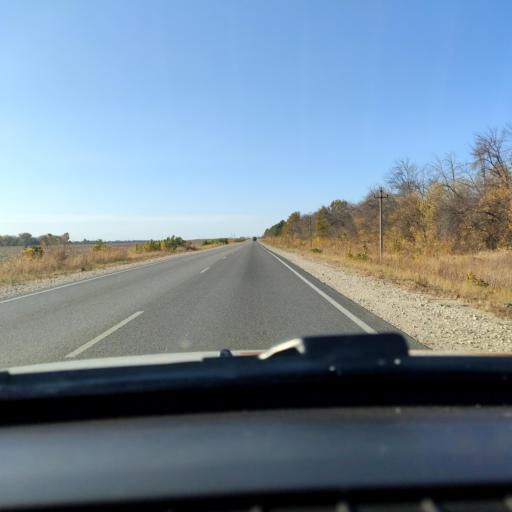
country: RU
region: Voronezj
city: Semiluki
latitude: 51.7301
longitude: 38.9759
